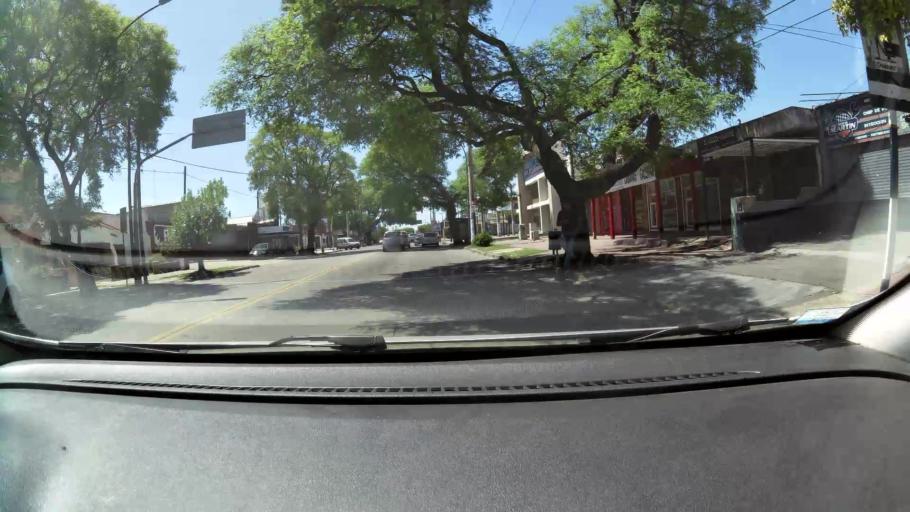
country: AR
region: Cordoba
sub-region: Departamento de Capital
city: Cordoba
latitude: -31.3772
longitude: -64.2069
